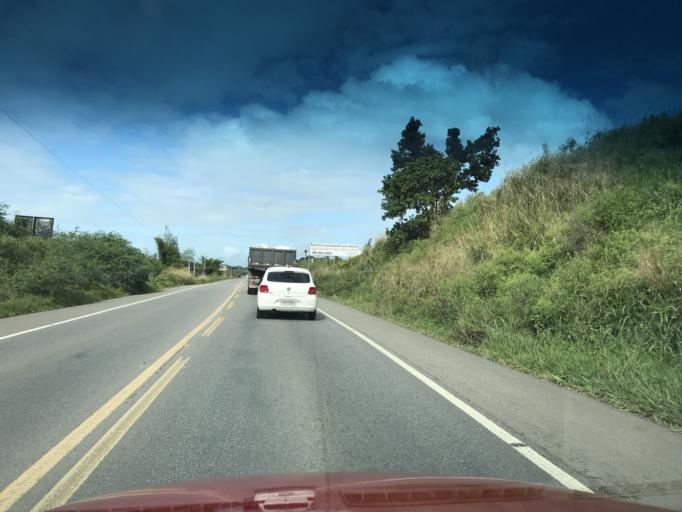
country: BR
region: Bahia
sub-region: Conceicao Do Almeida
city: Muritiba
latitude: -12.8970
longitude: -39.2351
